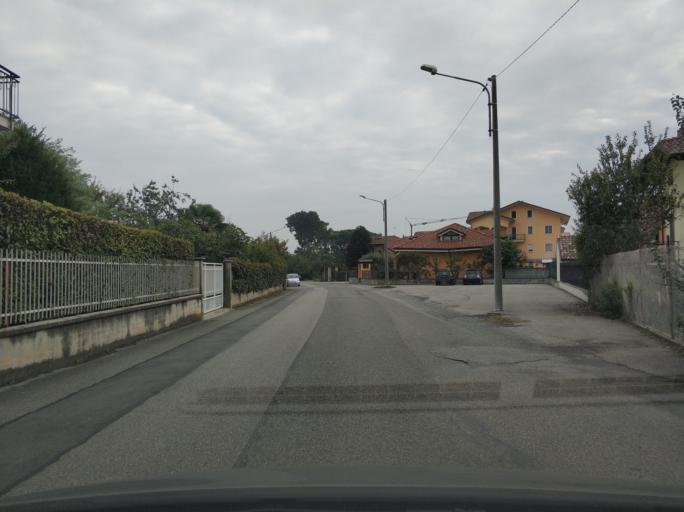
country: IT
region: Piedmont
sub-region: Provincia di Torino
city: Nole
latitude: 45.2383
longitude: 7.5701
